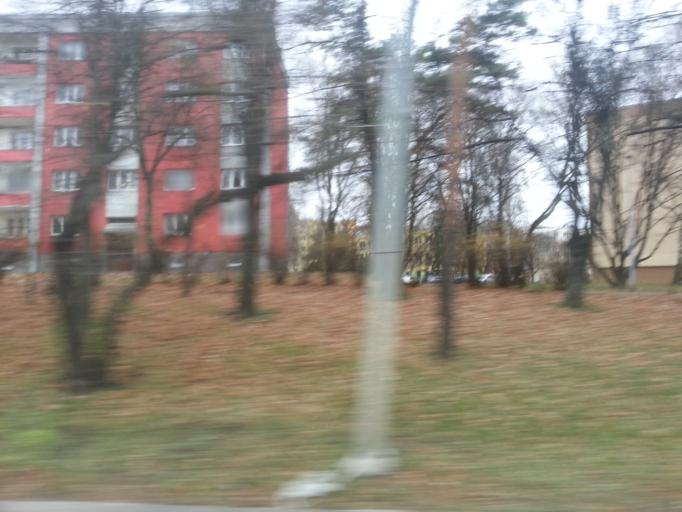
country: CZ
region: Central Bohemia
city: Horomerice
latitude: 50.0855
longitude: 14.3484
